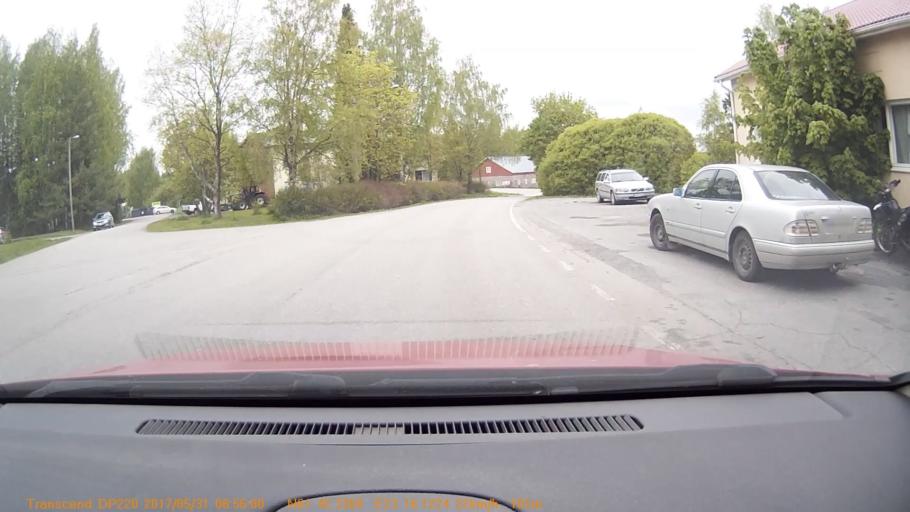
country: FI
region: Pirkanmaa
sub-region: Tampere
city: Viljakkala
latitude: 61.7055
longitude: 23.2689
